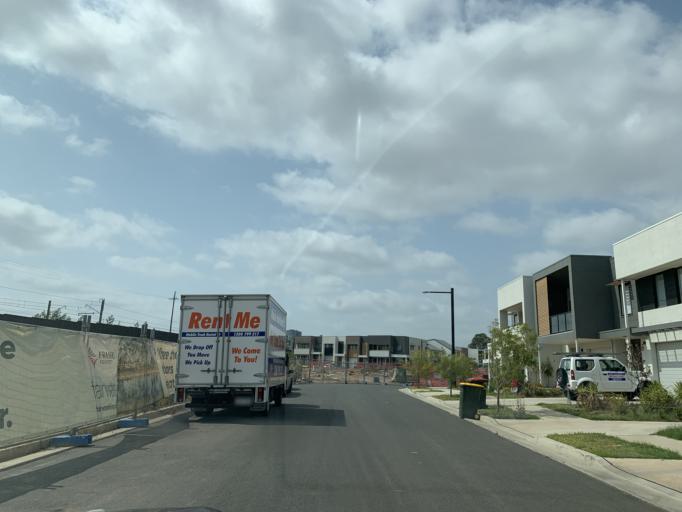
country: AU
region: New South Wales
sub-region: Blacktown
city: Blacktown
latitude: -33.7575
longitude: 150.9036
